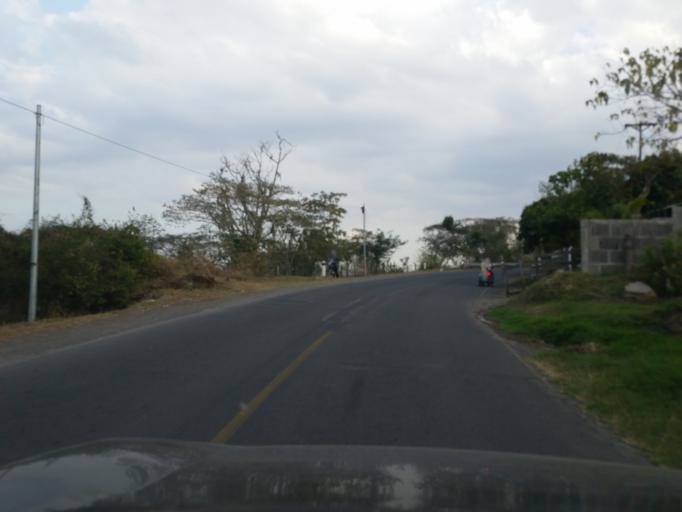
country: NI
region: Jinotega
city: San Rafael del Norte
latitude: 13.1703
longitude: -86.0661
